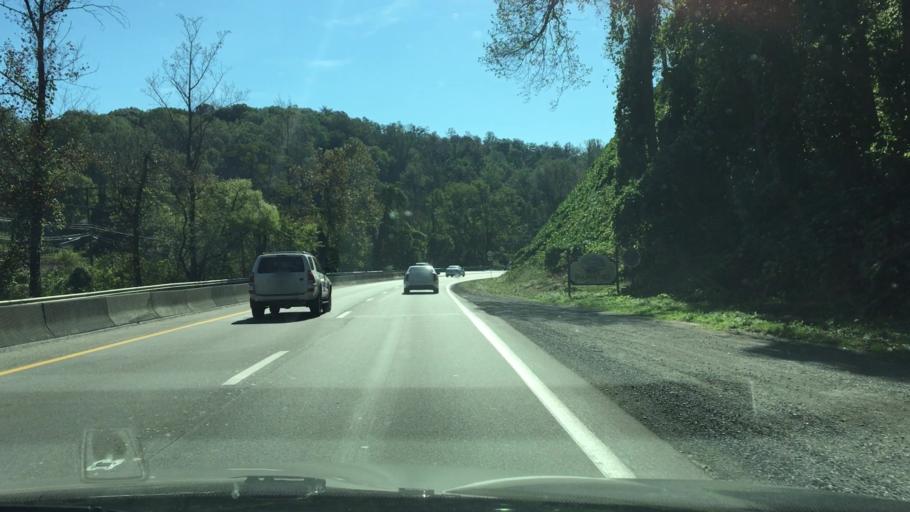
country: US
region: Virginia
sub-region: Roanoke County
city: Narrows
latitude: 37.1224
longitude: -79.9568
